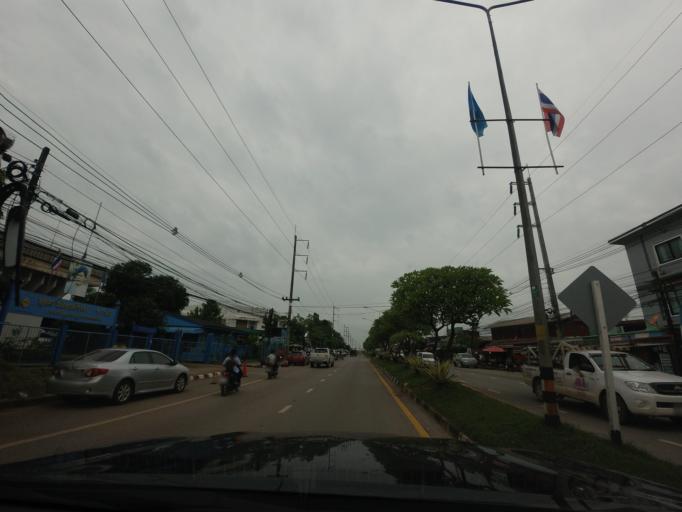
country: TH
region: Nong Khai
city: Tha Bo
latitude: 17.8474
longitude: 102.5775
